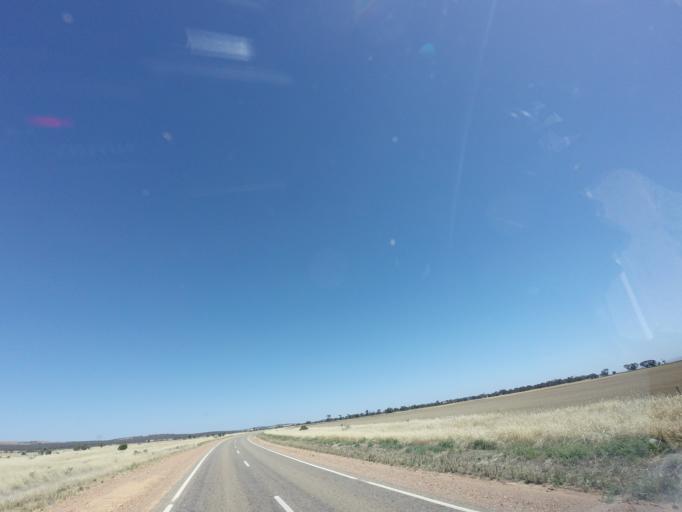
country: AU
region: South Australia
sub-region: Peterborough
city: Peterborough
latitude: -32.8505
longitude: 138.7338
